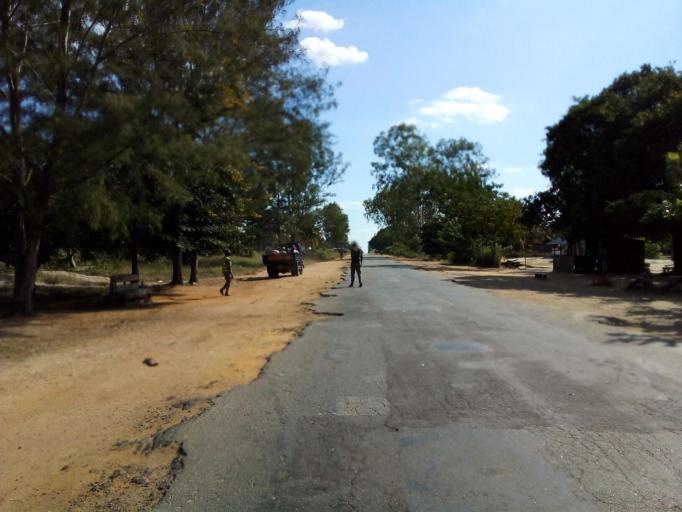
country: MZ
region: Zambezia
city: Quelimane
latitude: -17.5763
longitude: 36.6436
